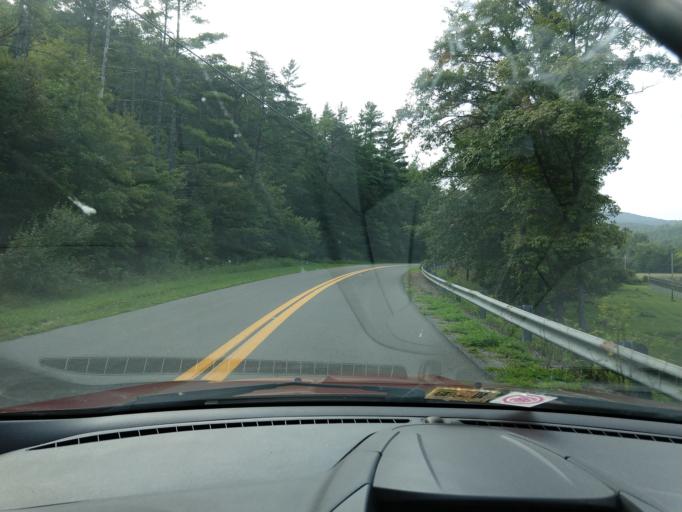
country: US
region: Virginia
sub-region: City of Covington
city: Covington
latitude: 37.9642
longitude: -80.1257
